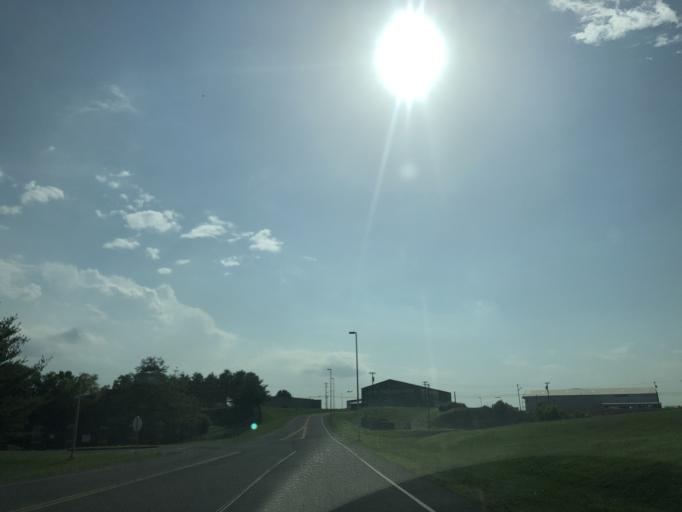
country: US
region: Tennessee
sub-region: Davidson County
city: Oak Hill
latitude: 36.1147
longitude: -86.6747
